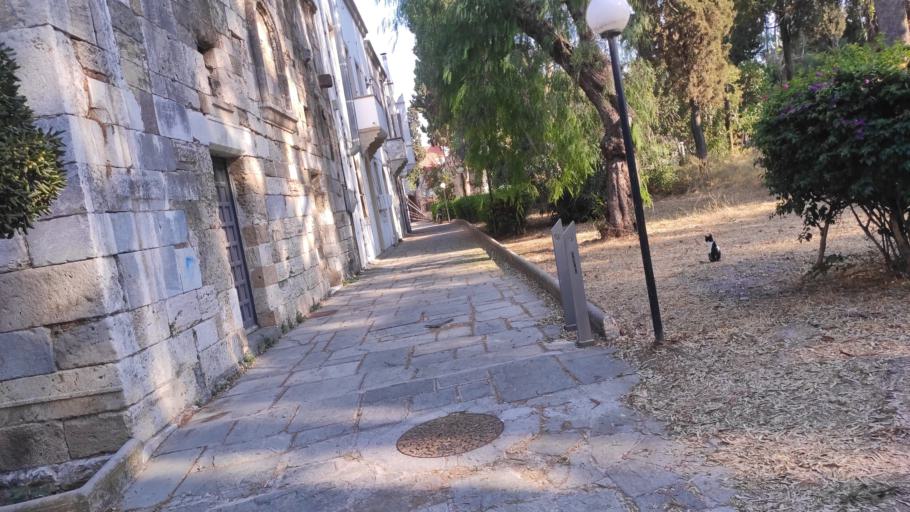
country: GR
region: South Aegean
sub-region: Nomos Dodekanisou
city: Kos
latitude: 36.8941
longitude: 27.2921
